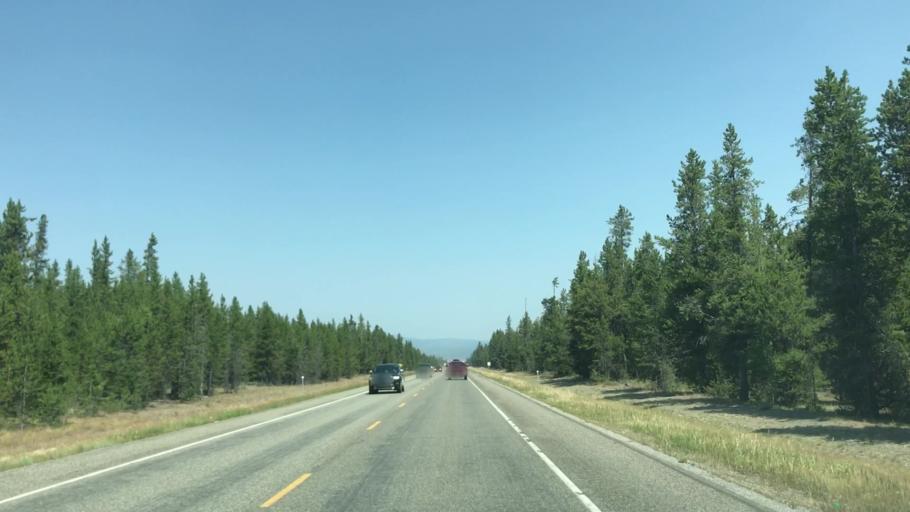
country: US
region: Montana
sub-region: Gallatin County
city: West Yellowstone
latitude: 44.6800
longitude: -111.1007
